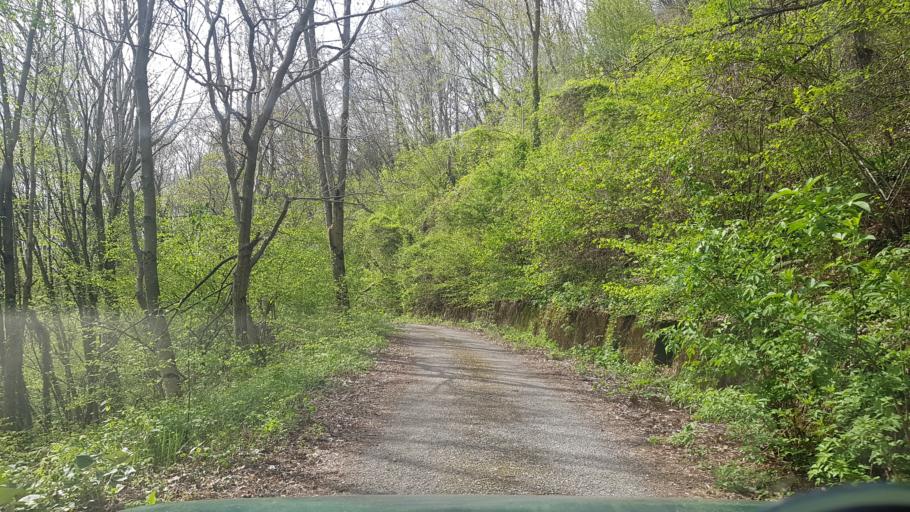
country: IT
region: Friuli Venezia Giulia
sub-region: Provincia di Udine
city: Attimis
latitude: 46.2102
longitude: 13.3422
